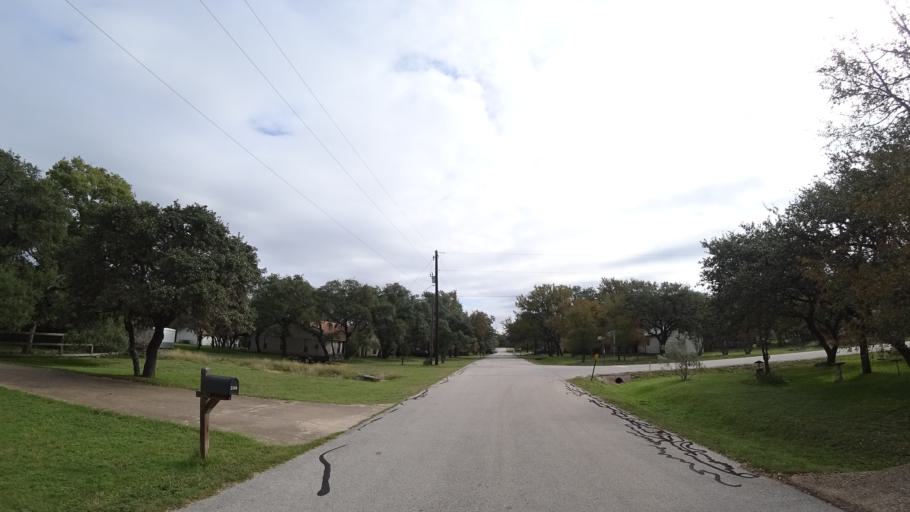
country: US
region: Texas
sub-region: Travis County
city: Shady Hollow
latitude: 30.1390
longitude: -97.8875
